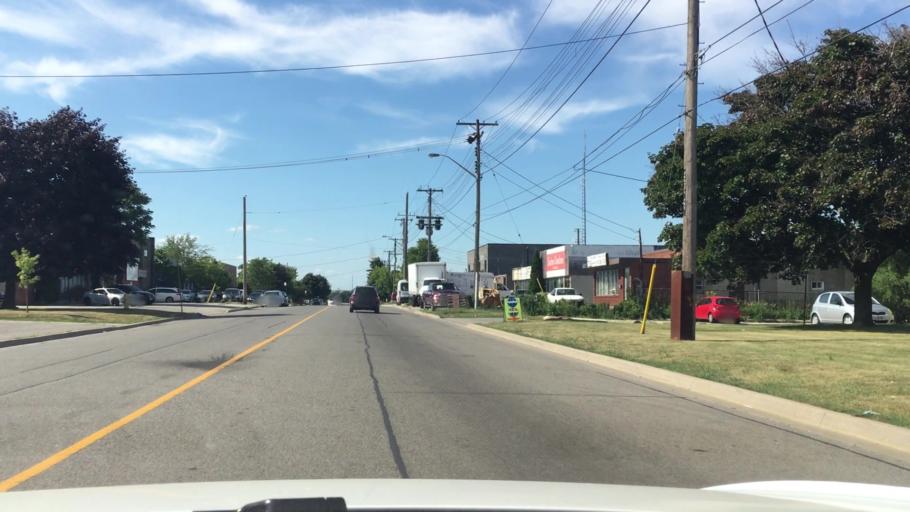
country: CA
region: Ontario
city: Scarborough
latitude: 43.7510
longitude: -79.2897
